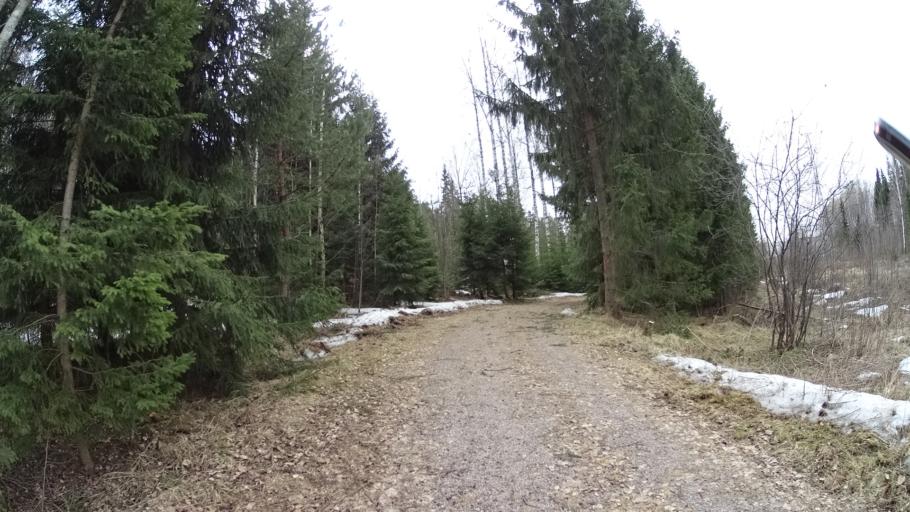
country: FI
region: Uusimaa
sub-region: Helsinki
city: Vantaa
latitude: 60.2984
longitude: 24.9377
